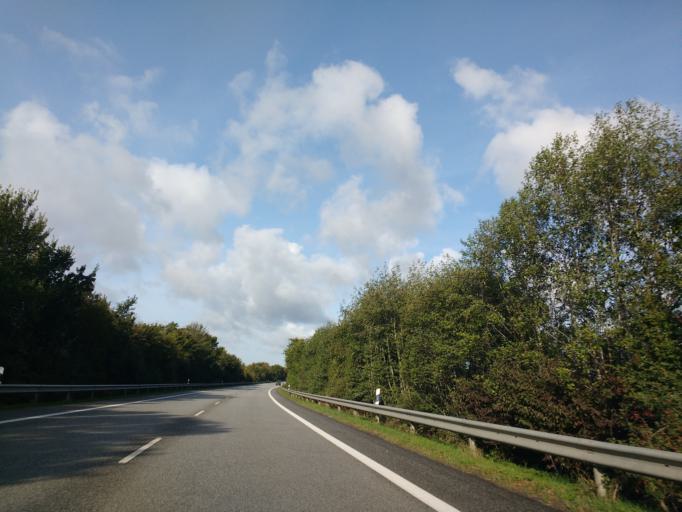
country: DE
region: Schleswig-Holstein
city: Altenkrempe
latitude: 54.1223
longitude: 10.8342
